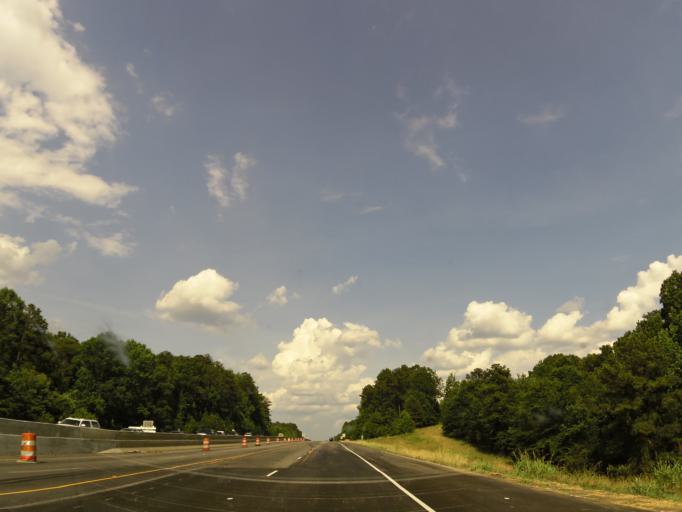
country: US
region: Alabama
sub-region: Tuscaloosa County
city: Coaling
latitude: 33.1764
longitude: -87.3900
